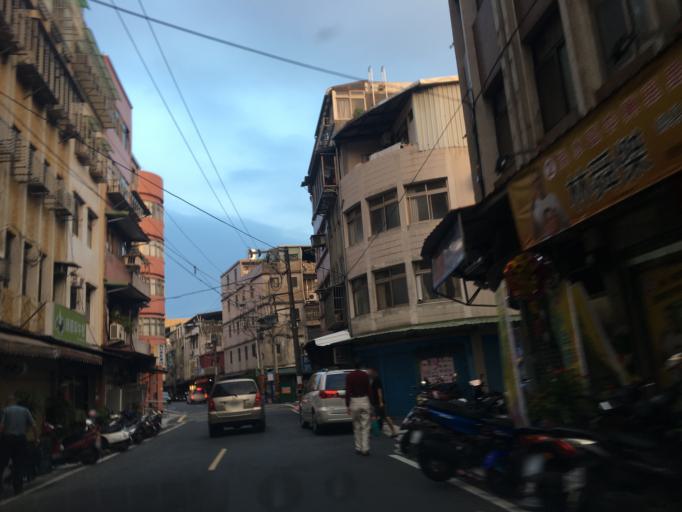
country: TW
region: Taipei
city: Taipei
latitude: 25.1724
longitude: 121.4426
